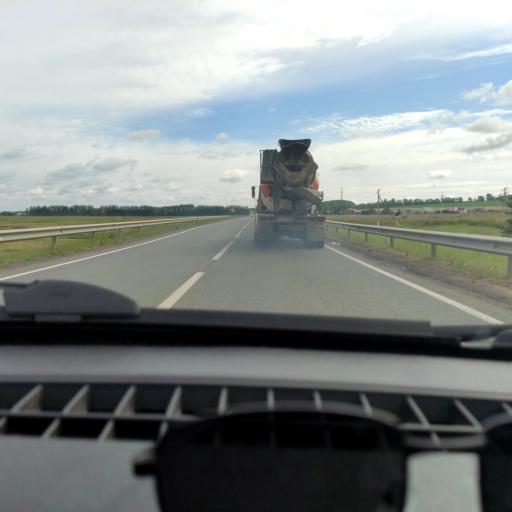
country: RU
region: Bashkortostan
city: Karmaskaly
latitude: 54.3842
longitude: 56.2245
